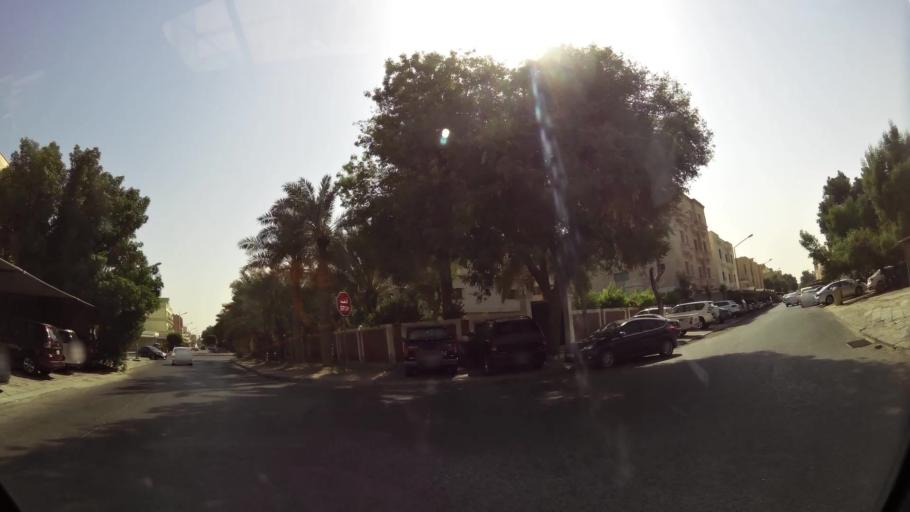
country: KW
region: Muhafazat Hawalli
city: Salwa
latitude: 29.2870
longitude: 48.0853
